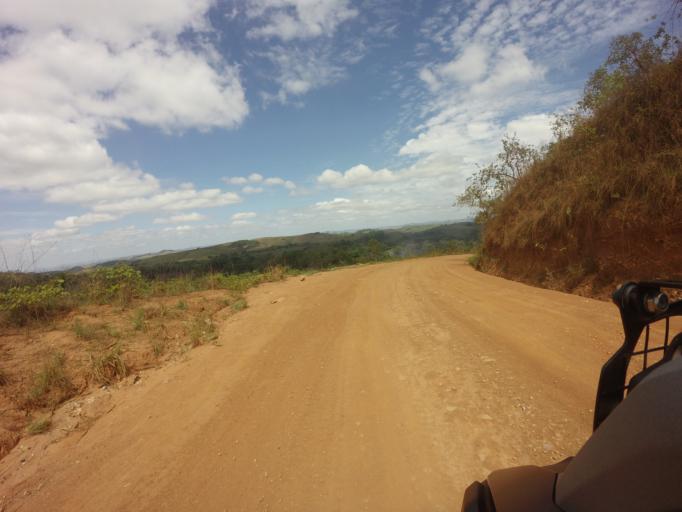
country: CD
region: Bas-Congo
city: Matadi
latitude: -5.9936
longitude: 13.5510
